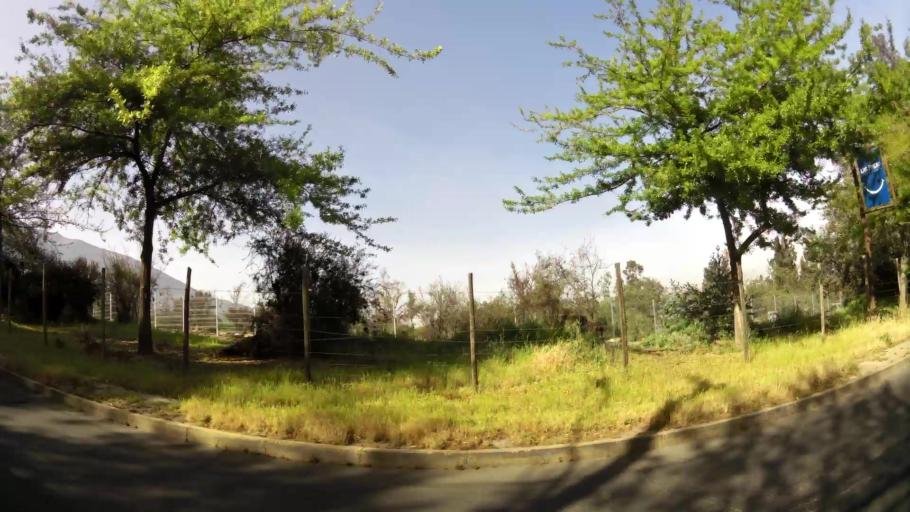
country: CL
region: Santiago Metropolitan
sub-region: Provincia de Santiago
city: Villa Presidente Frei, Nunoa, Santiago, Chile
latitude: -33.5010
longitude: -70.5362
